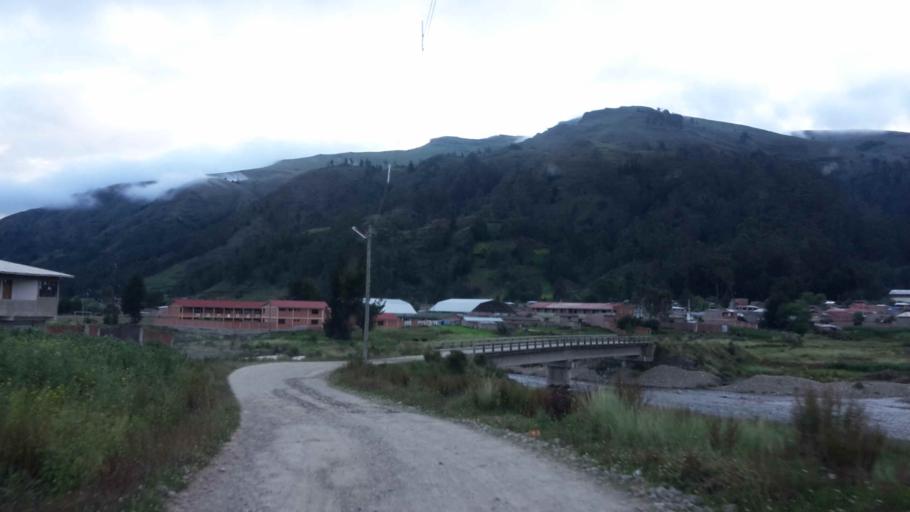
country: BO
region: Cochabamba
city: Colomi
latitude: -17.2718
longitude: -65.9234
